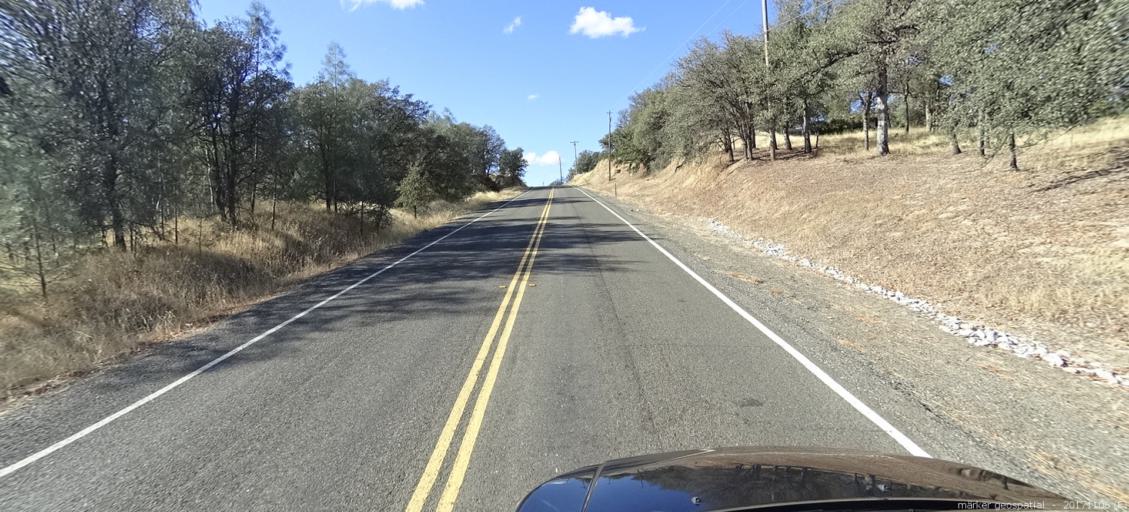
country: US
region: California
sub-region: Shasta County
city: Palo Cedro
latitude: 40.5928
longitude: -122.2521
